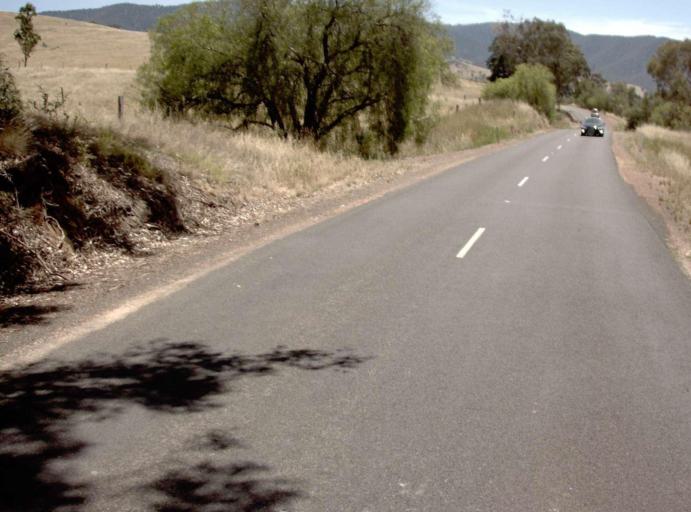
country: AU
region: Victoria
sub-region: East Gippsland
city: Bairnsdale
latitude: -37.2073
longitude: 147.7183
